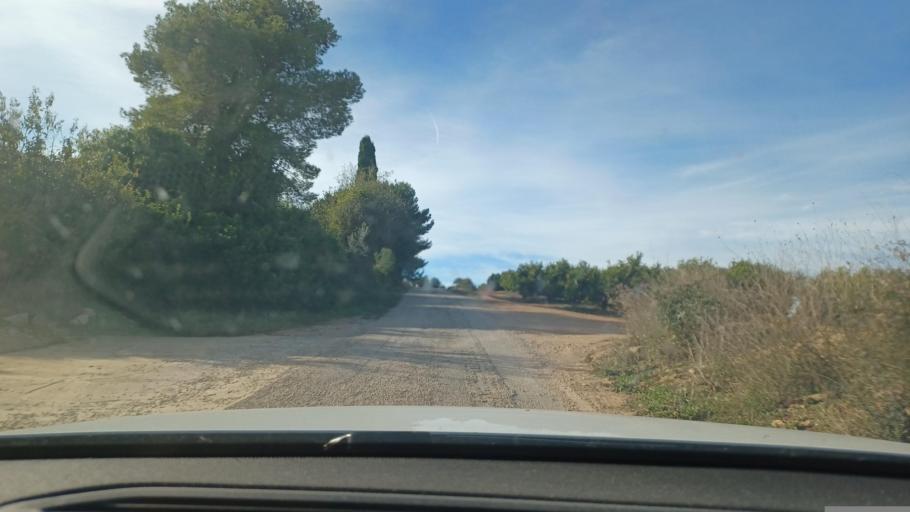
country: ES
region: Catalonia
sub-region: Provincia de Tarragona
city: Santa Barbara
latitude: 40.6878
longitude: 0.5023
